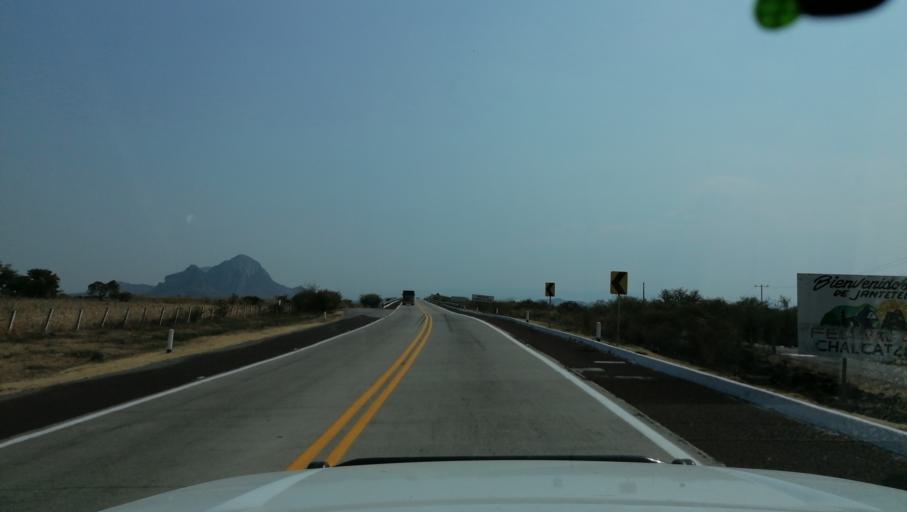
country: MX
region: Morelos
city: Jantetelco
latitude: 18.7190
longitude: -98.7676
